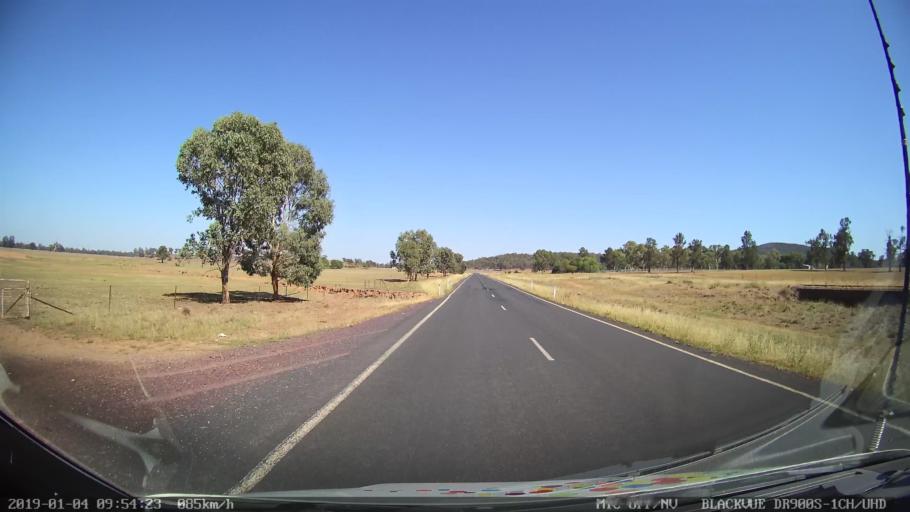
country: AU
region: New South Wales
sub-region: Cabonne
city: Canowindra
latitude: -33.5418
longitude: 148.4155
